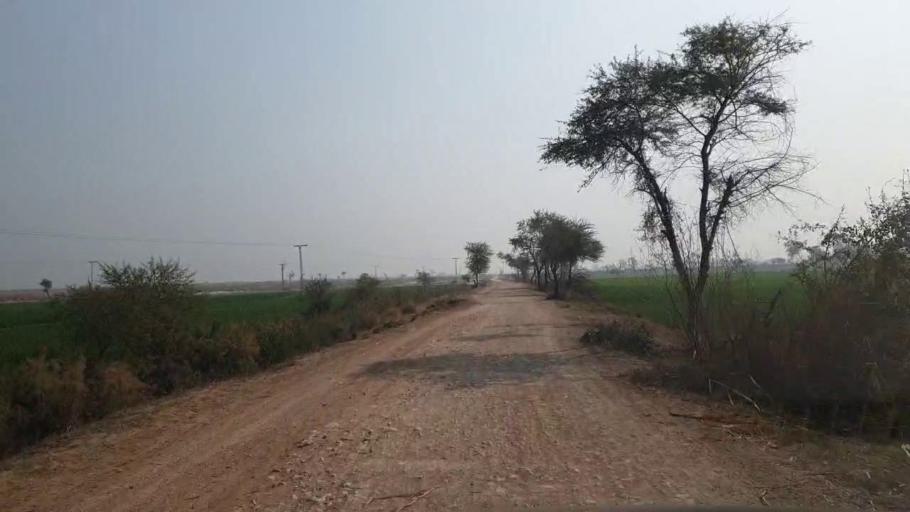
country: PK
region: Sindh
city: Hala
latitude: 25.9317
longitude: 68.4725
